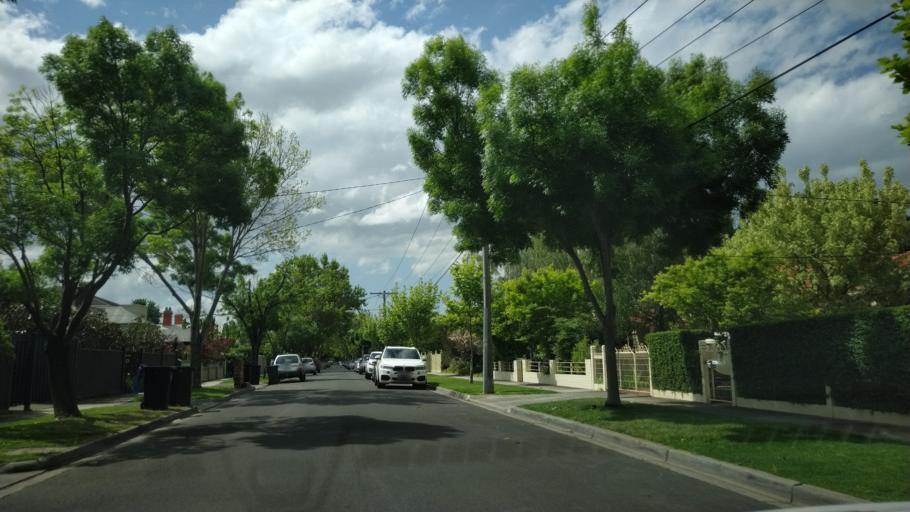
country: AU
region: Victoria
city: Glen Huntly
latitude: -37.8816
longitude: 145.0559
